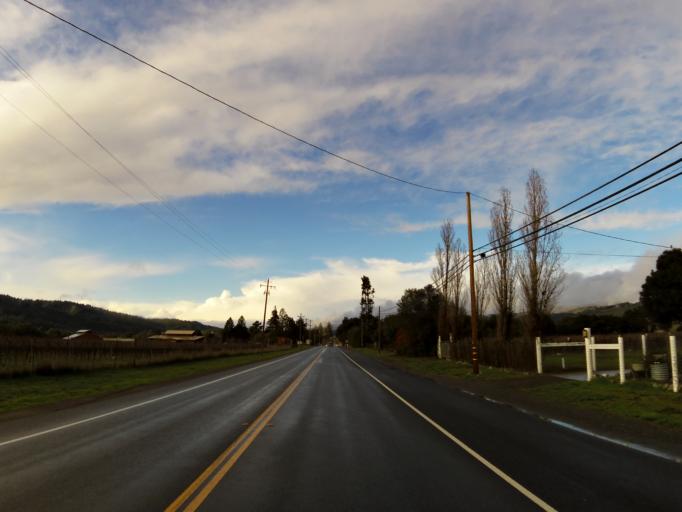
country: US
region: California
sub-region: Mendocino County
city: Boonville
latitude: 39.0007
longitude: -123.3597
